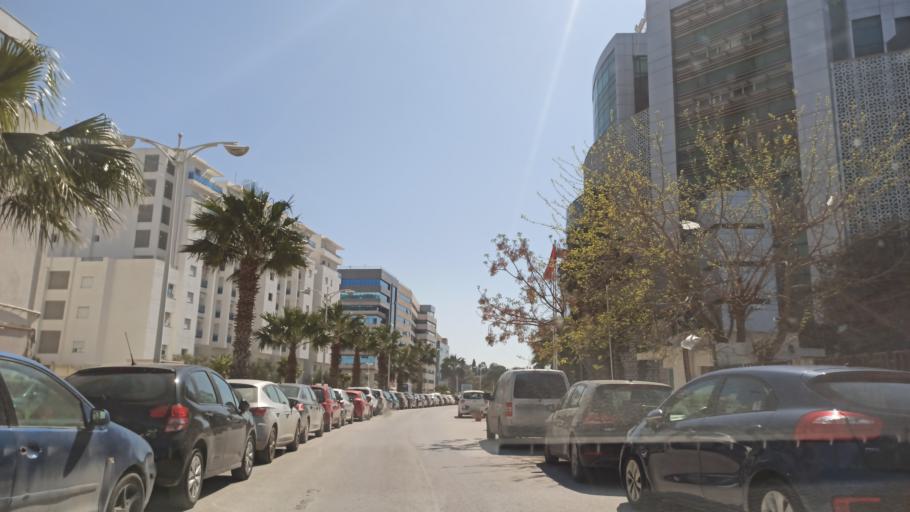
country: TN
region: Ariana
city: Ariana
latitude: 36.8497
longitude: 10.1967
